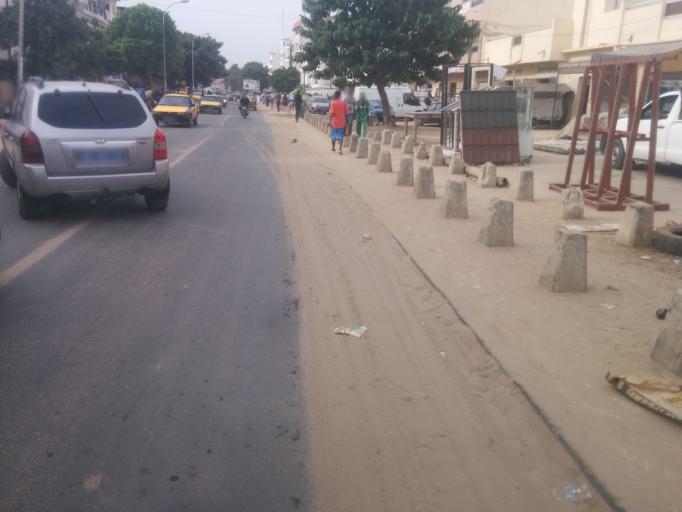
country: SN
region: Dakar
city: Grand Dakar
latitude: 14.7372
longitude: -17.4551
